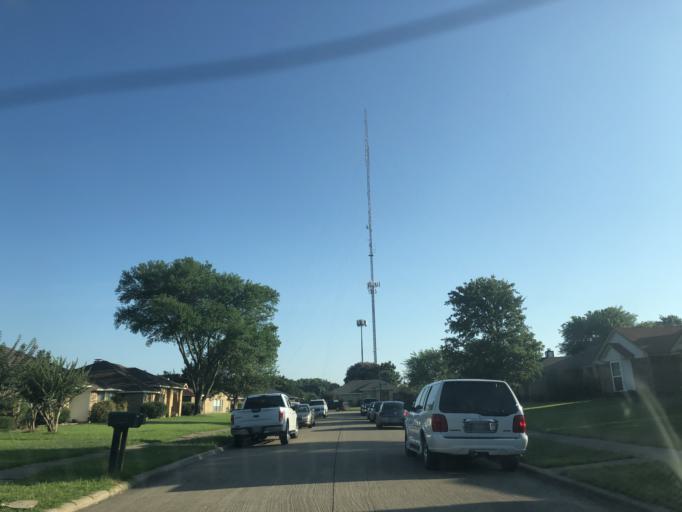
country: US
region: Texas
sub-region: Dallas County
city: Sunnyvale
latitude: 32.8415
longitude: -96.5638
